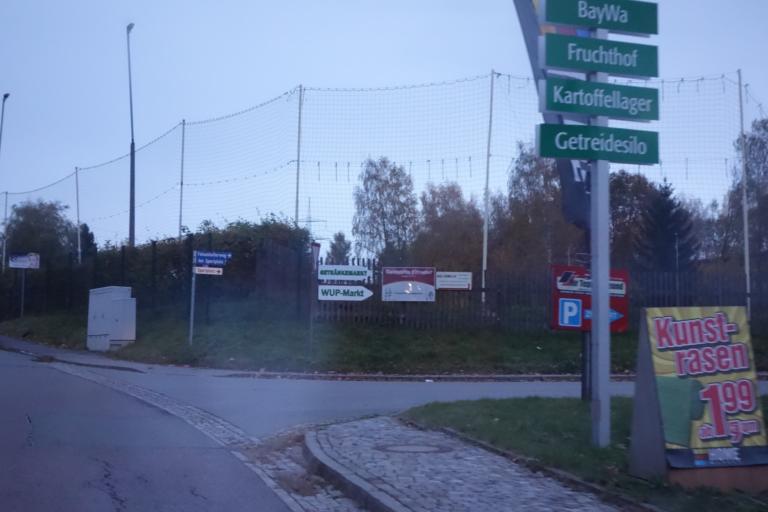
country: DE
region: Saxony
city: Mildenau
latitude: 50.5988
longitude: 13.0733
